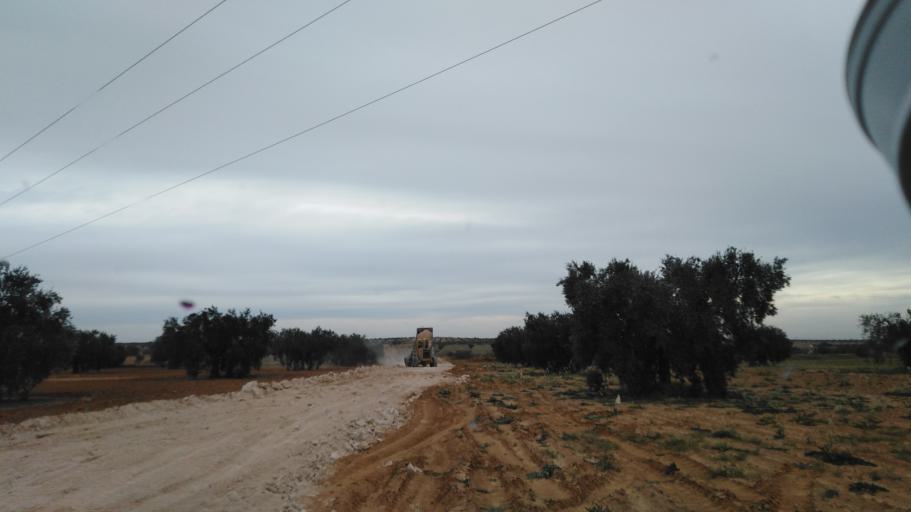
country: TN
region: Safaqis
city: Bi'r `Ali Bin Khalifah
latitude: 34.7702
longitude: 10.3737
